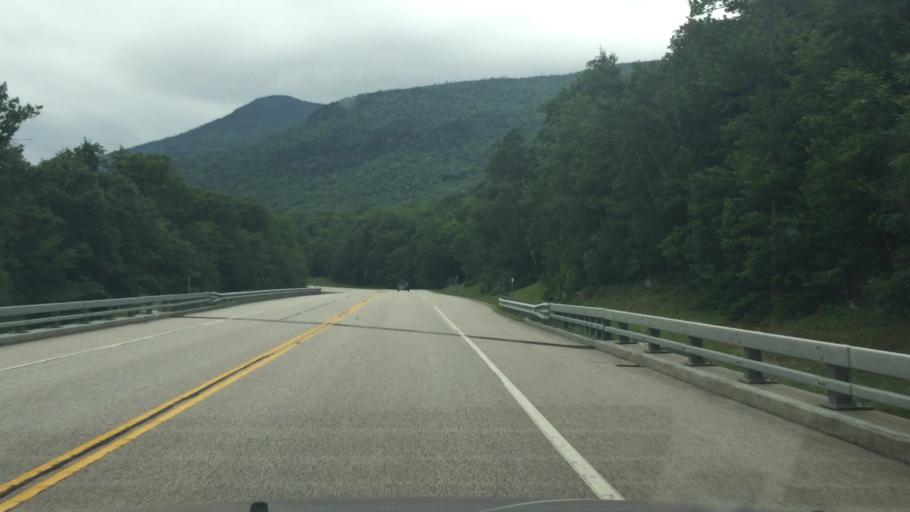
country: US
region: New Hampshire
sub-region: Carroll County
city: North Conway
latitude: 44.1532
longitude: -71.3647
